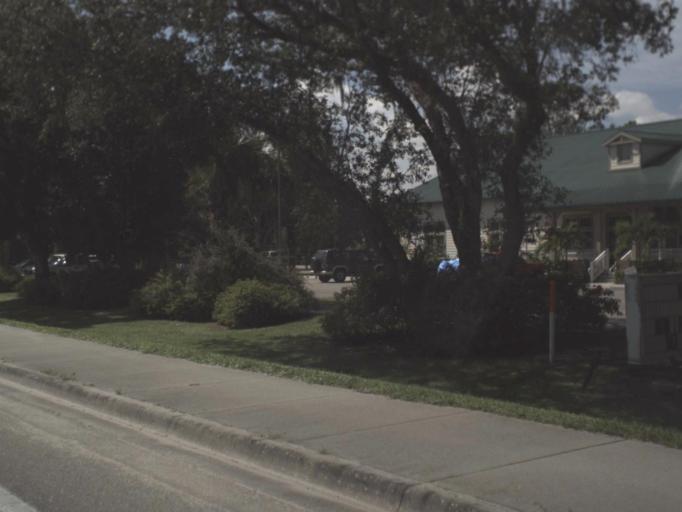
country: US
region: Florida
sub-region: Hendry County
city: LaBelle
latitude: 26.7552
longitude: -81.4383
